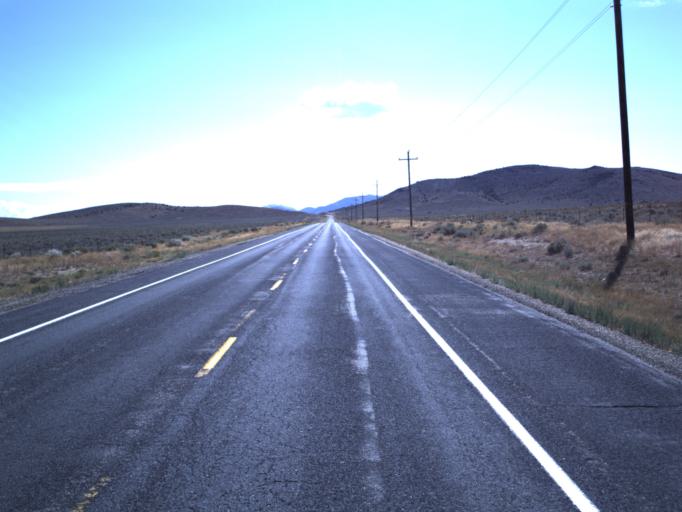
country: US
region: Utah
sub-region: Utah County
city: Eagle Mountain
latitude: 40.0792
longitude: -112.3997
